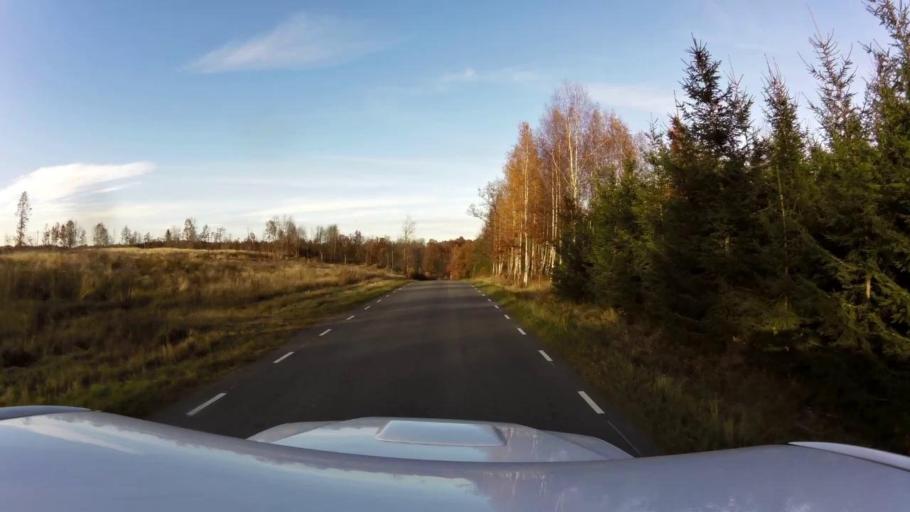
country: SE
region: OEstergoetland
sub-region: Linkopings Kommun
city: Sturefors
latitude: 58.2576
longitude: 15.6635
